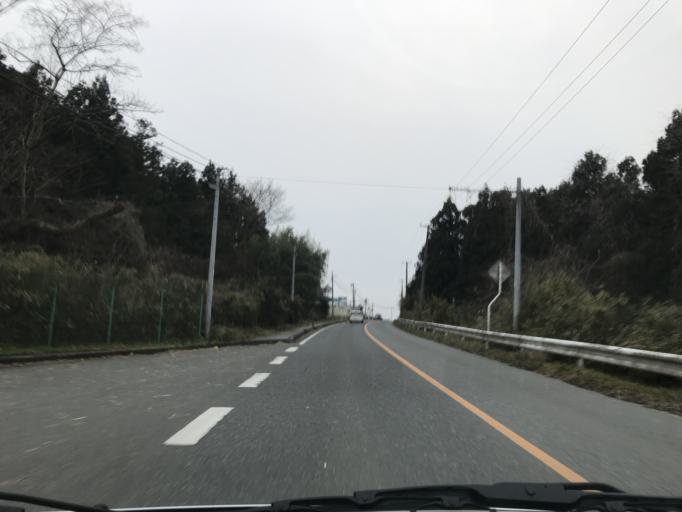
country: JP
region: Miyagi
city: Wakuya
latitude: 38.6943
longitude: 141.1481
